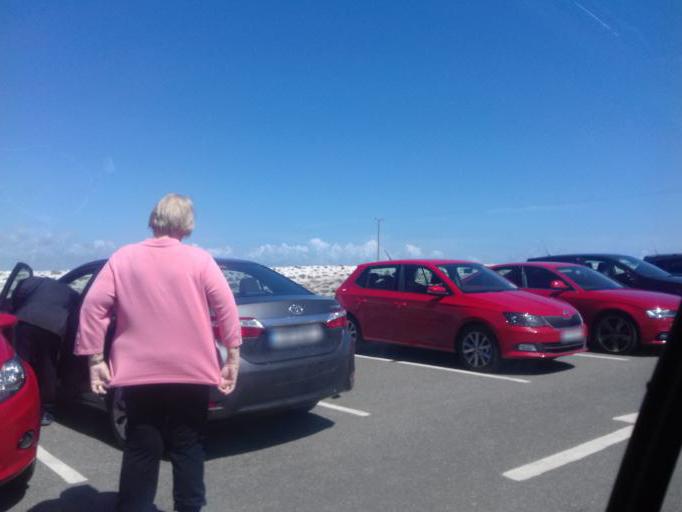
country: IE
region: Munster
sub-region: Waterford
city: Dunmore East
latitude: 52.1248
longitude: -6.9292
